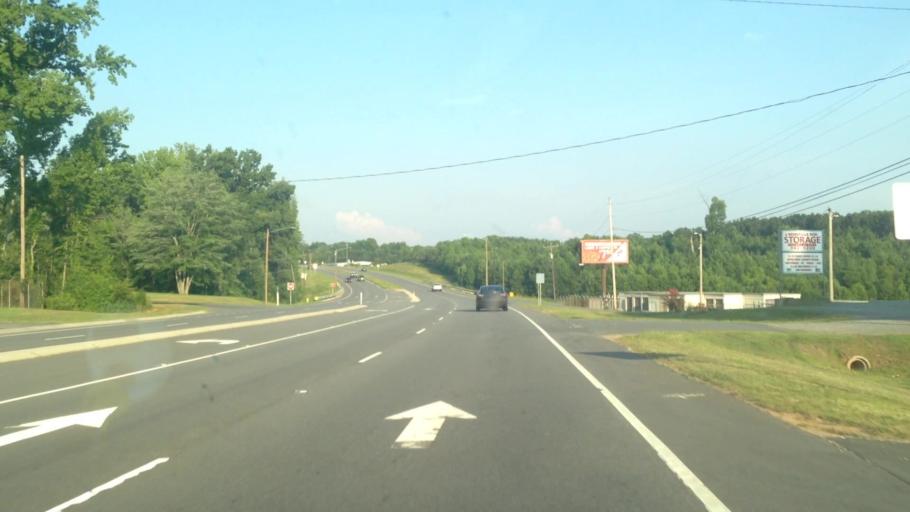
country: US
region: North Carolina
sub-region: Rockingham County
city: Reidsville
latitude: 36.3173
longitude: -79.6800
